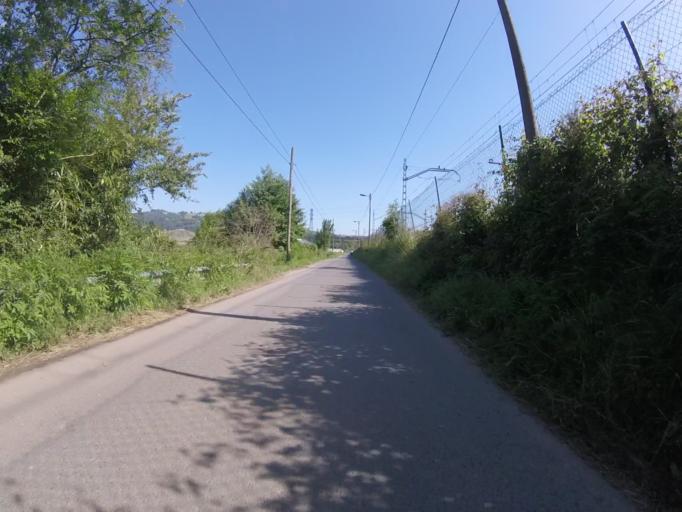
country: ES
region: Basque Country
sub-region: Provincia de Guipuzcoa
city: Astigarraga
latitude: 43.2909
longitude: -1.9558
